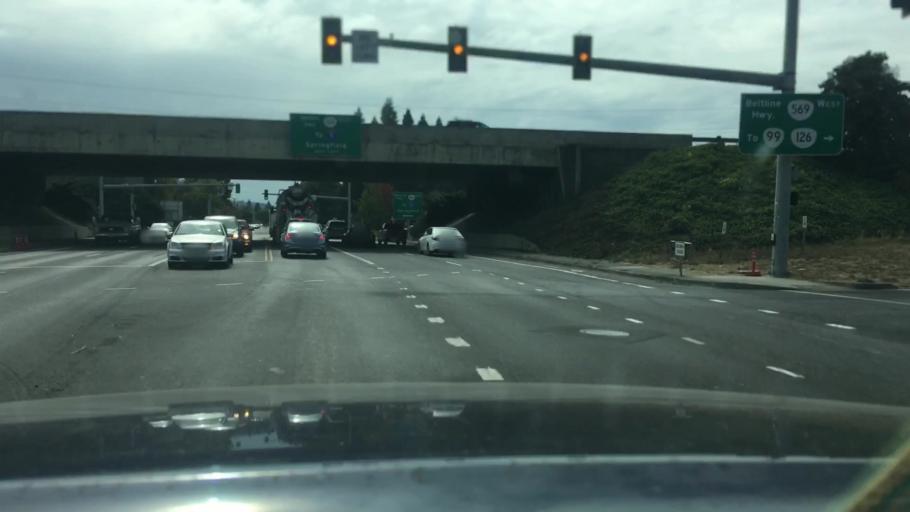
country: US
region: Oregon
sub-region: Lane County
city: Eugene
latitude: 44.0882
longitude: -123.0677
